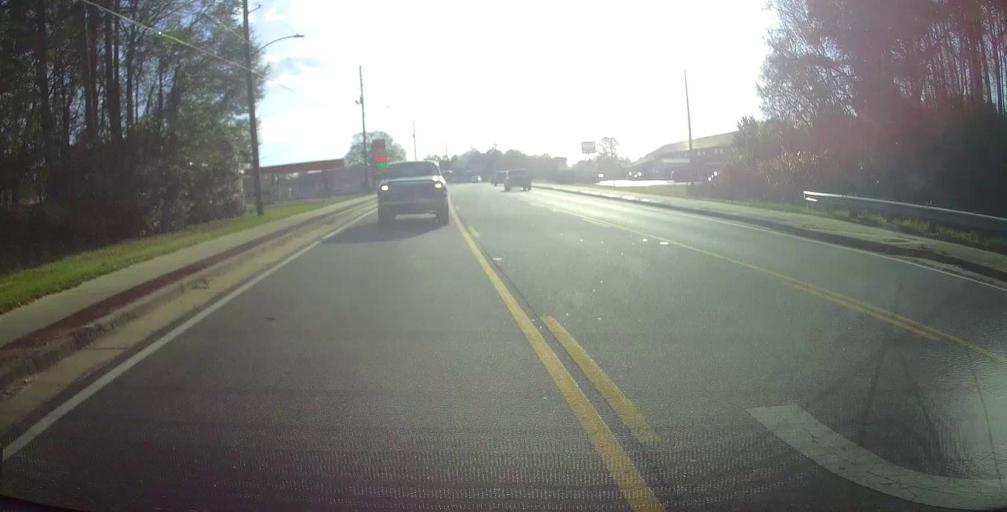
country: US
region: Georgia
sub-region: Tattnall County
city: Reidsville
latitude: 32.0820
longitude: -82.1236
